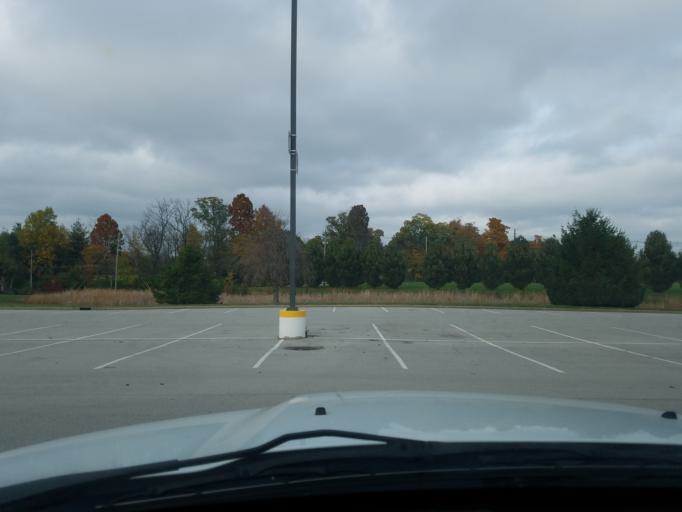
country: US
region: Kentucky
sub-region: Jefferson County
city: Douglass Hills
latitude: 38.2294
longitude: -85.5446
